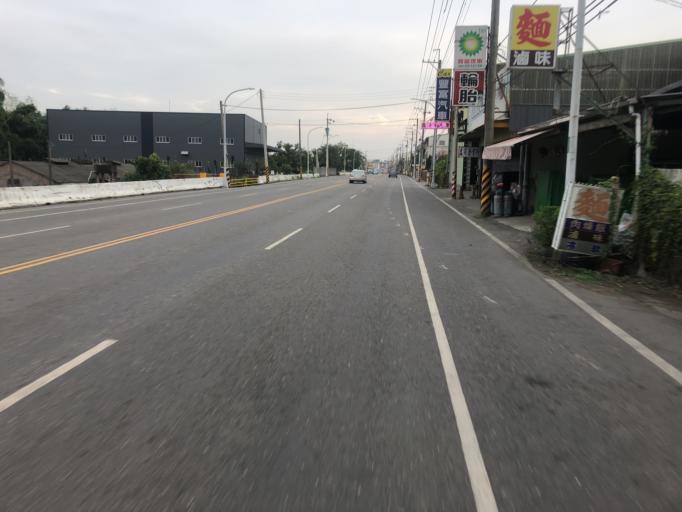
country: TW
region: Taiwan
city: Xinying
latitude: 23.1447
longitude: 120.2880
